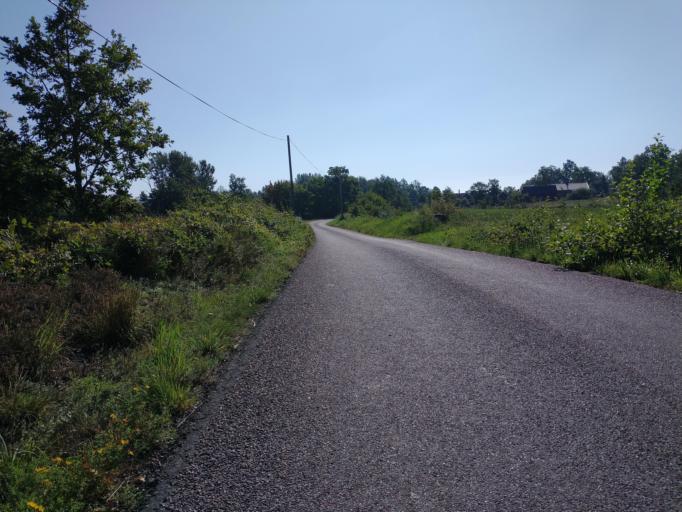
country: SE
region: Kalmar
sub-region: Kalmar Kommun
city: Lindsdal
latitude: 56.7882
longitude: 16.2907
